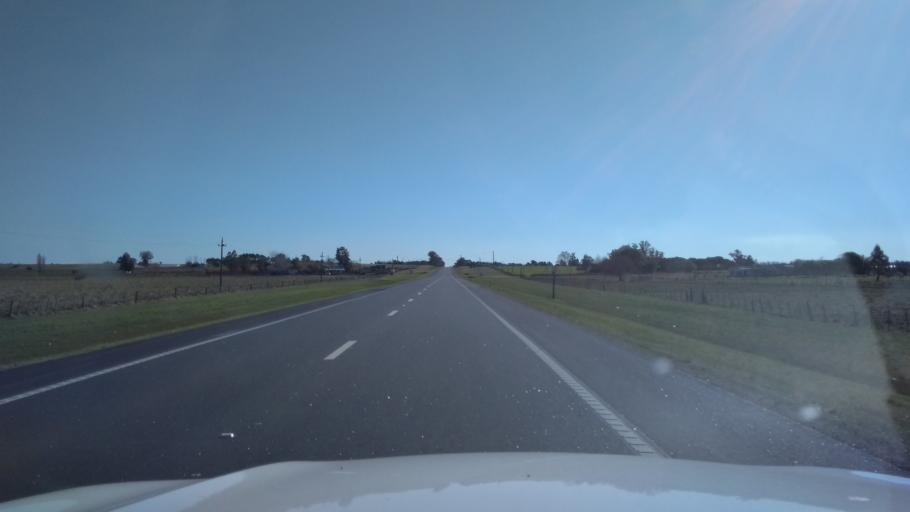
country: UY
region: Canelones
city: San Jacinto
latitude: -34.5270
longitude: -55.9586
